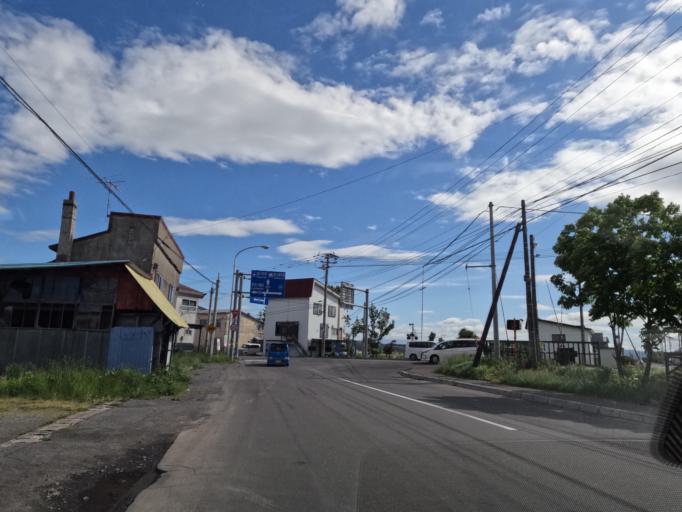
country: JP
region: Hokkaido
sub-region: Asahikawa-shi
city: Asahikawa
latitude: 43.8227
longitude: 142.5169
